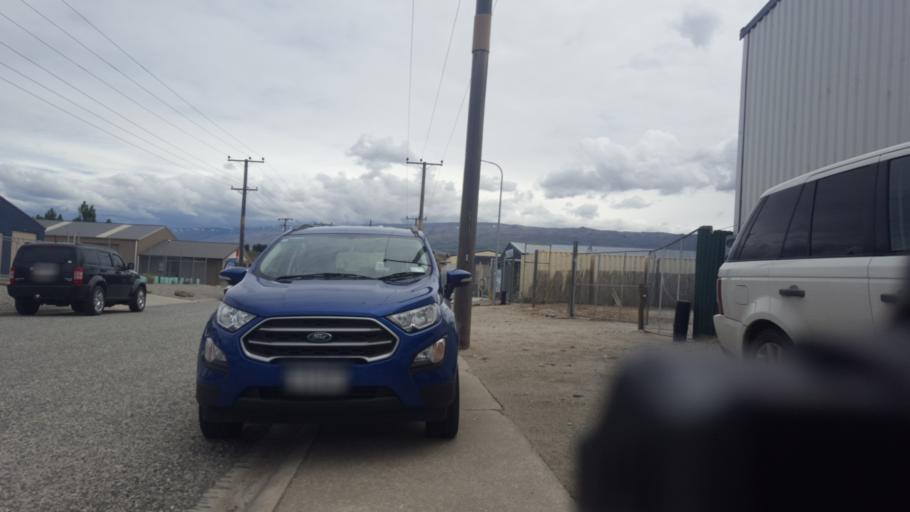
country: NZ
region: Otago
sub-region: Queenstown-Lakes District
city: Wanaka
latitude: -45.2487
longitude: 169.3735
